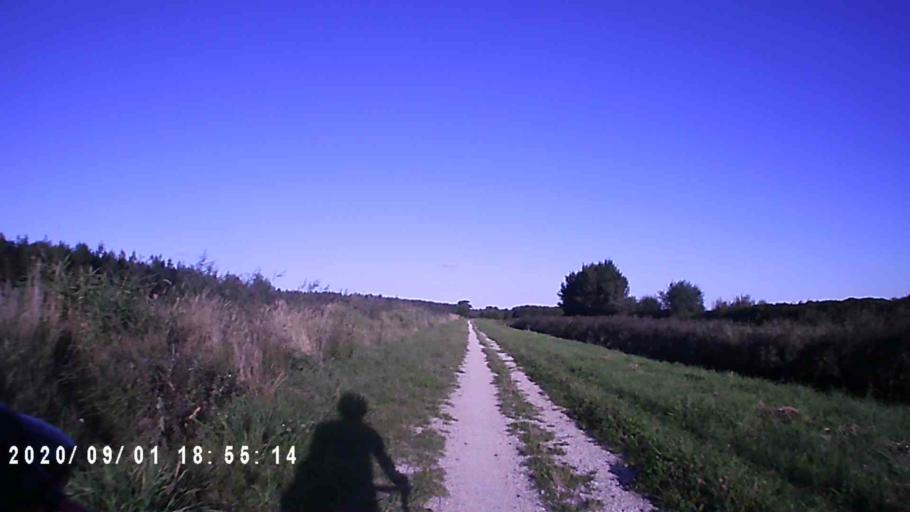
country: NL
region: Groningen
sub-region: Gemeente Veendam
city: Veendam
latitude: 53.1301
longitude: 6.8483
